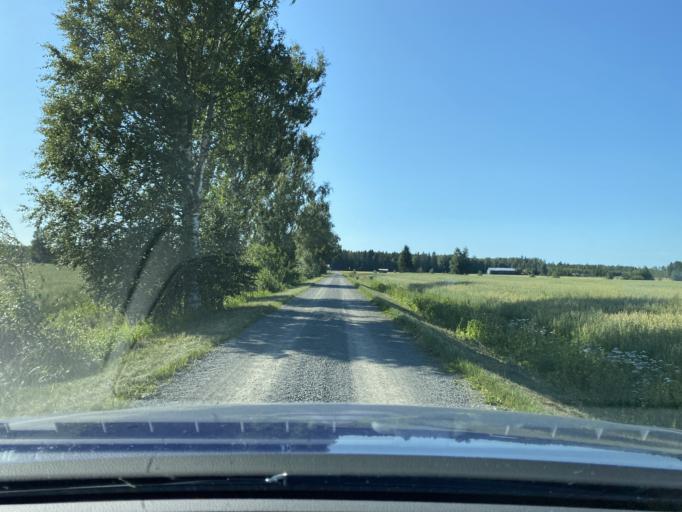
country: FI
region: Satakunta
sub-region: Rauma
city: Kiukainen
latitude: 61.1486
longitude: 22.0046
